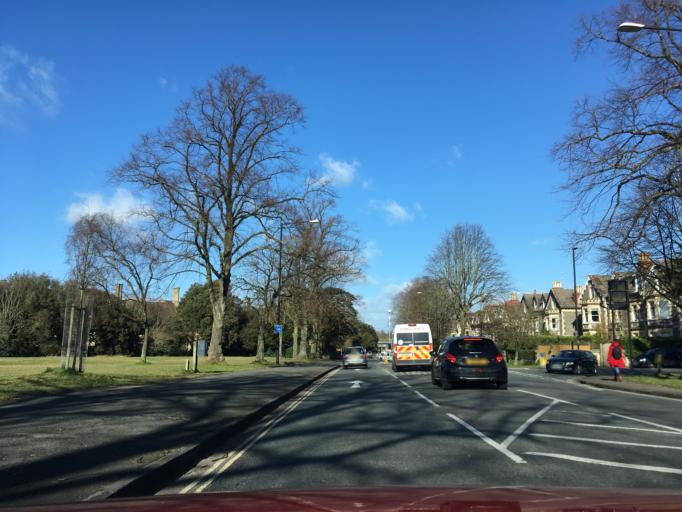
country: GB
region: England
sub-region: Bristol
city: Bristol
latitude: 51.4820
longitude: -2.6167
